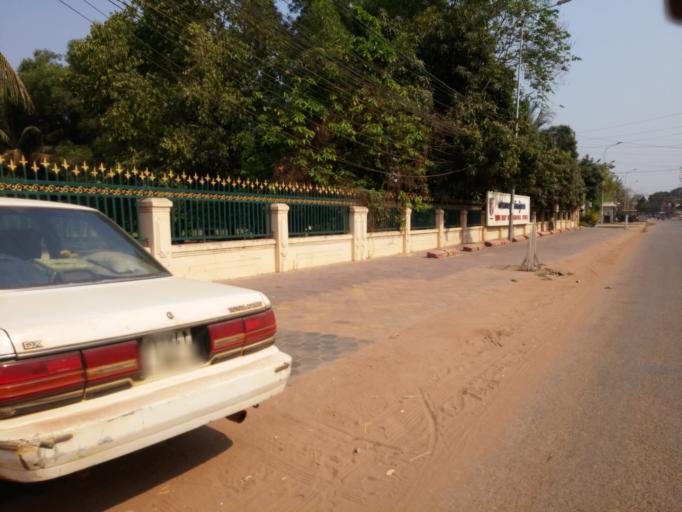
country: KH
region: Siem Reap
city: Siem Reap
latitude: 13.3739
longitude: 103.8503
